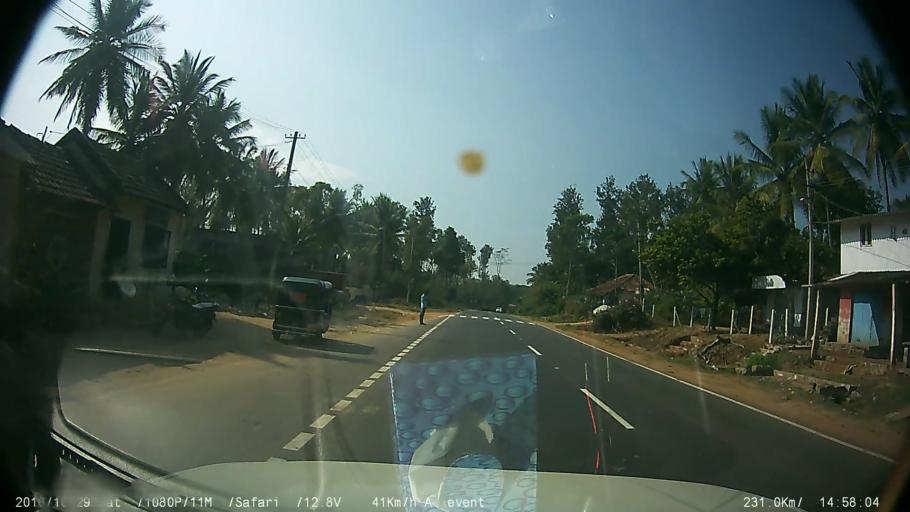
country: IN
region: Karnataka
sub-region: Kodagu
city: Suntikoppa
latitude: 12.4385
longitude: 75.8754
